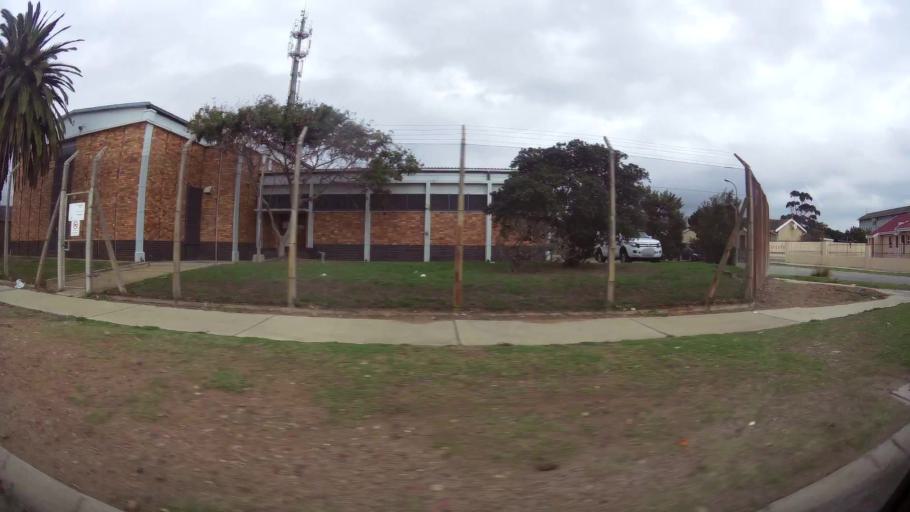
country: ZA
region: Eastern Cape
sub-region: Nelson Mandela Bay Metropolitan Municipality
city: Port Elizabeth
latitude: -33.9008
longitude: 25.5598
